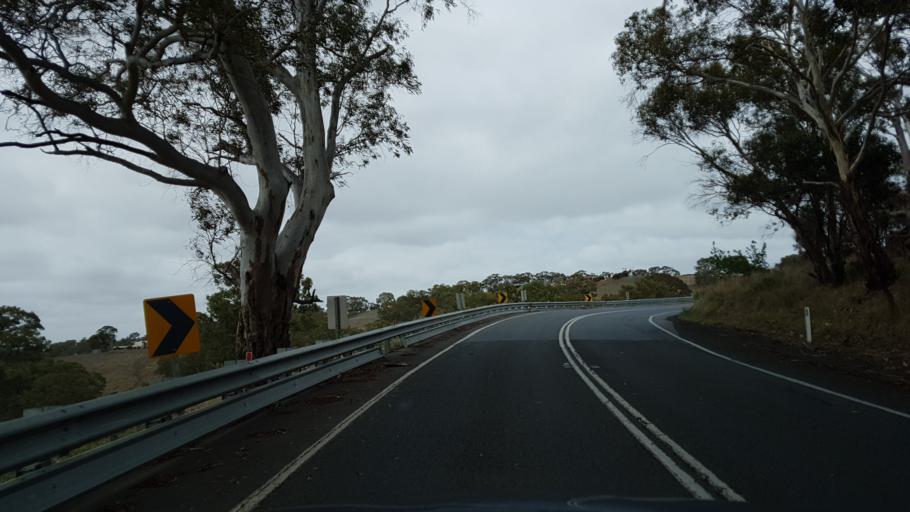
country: AU
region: South Australia
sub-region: Mount Barker
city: Nairne
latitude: -35.0432
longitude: 138.9450
